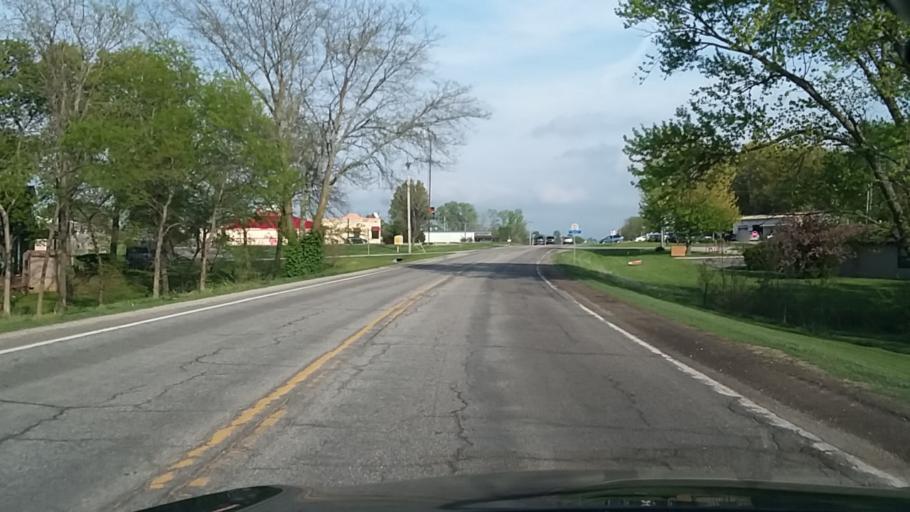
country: US
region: Kansas
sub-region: Douglas County
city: Baldwin City
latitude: 38.7818
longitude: -95.1805
